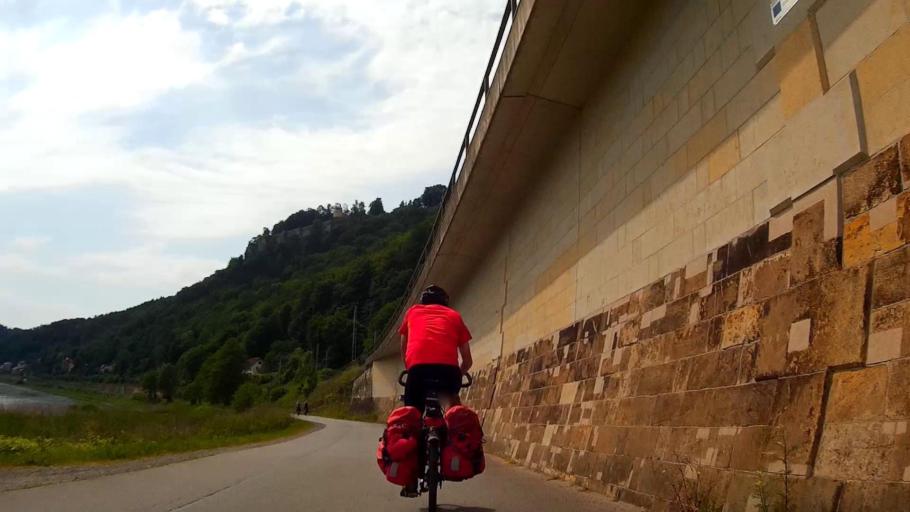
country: DE
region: Saxony
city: Konigstein
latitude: 50.9274
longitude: 14.0558
